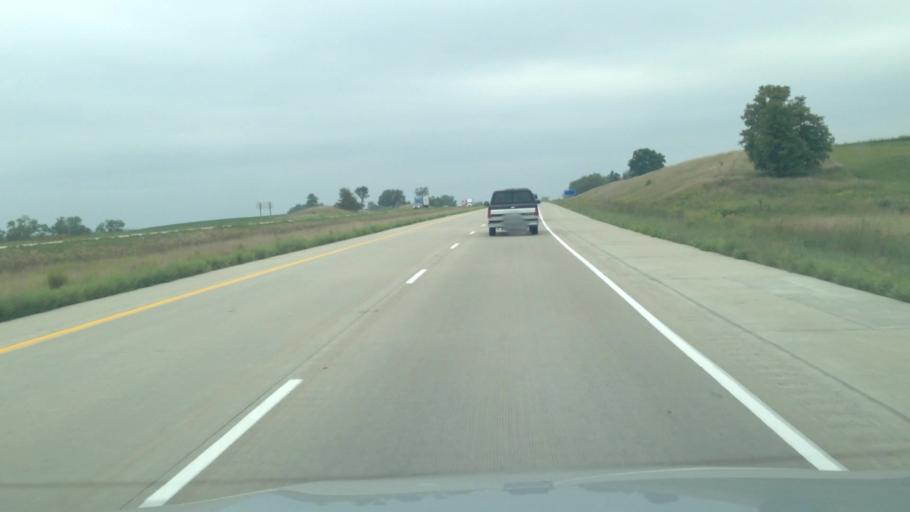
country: US
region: Iowa
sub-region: Decatur County
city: Lamoni
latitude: 40.5917
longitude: -93.9202
